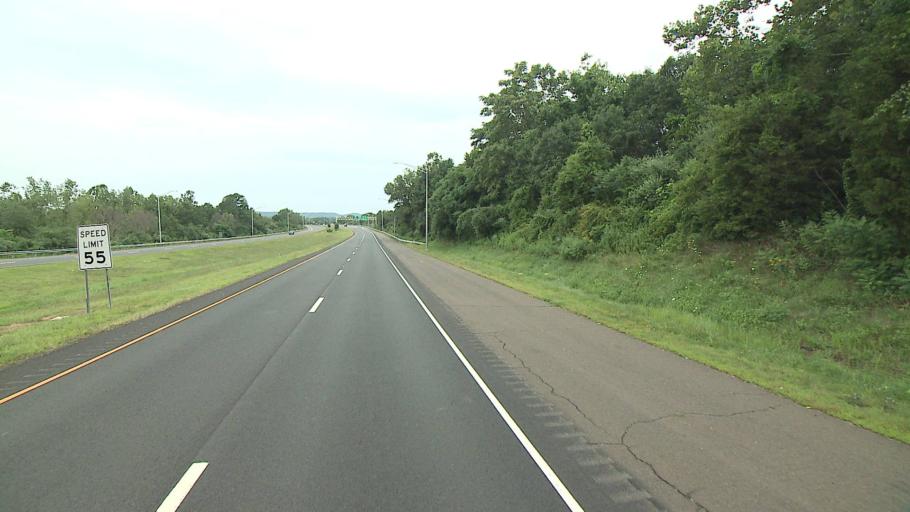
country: US
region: Connecticut
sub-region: New Haven County
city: Hamden
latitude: 41.3859
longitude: -72.8856
